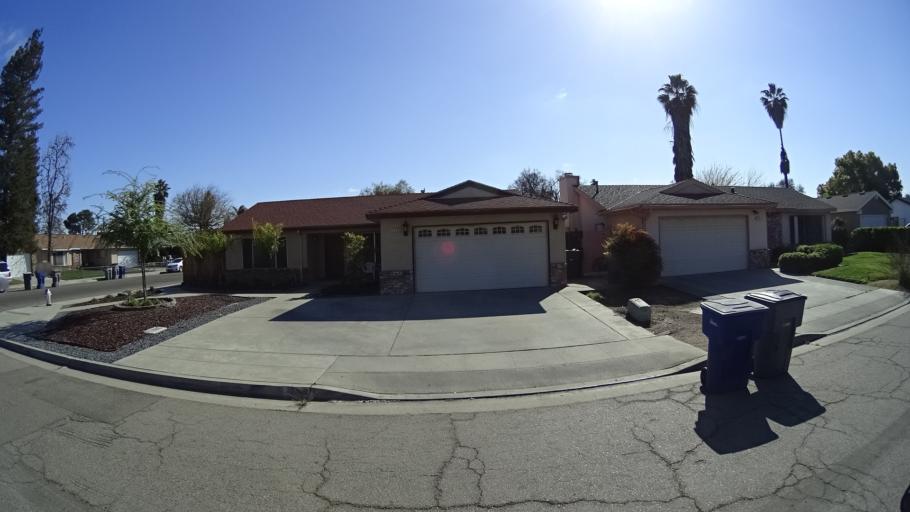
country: US
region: California
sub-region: Fresno County
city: West Park
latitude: 36.7985
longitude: -119.8845
